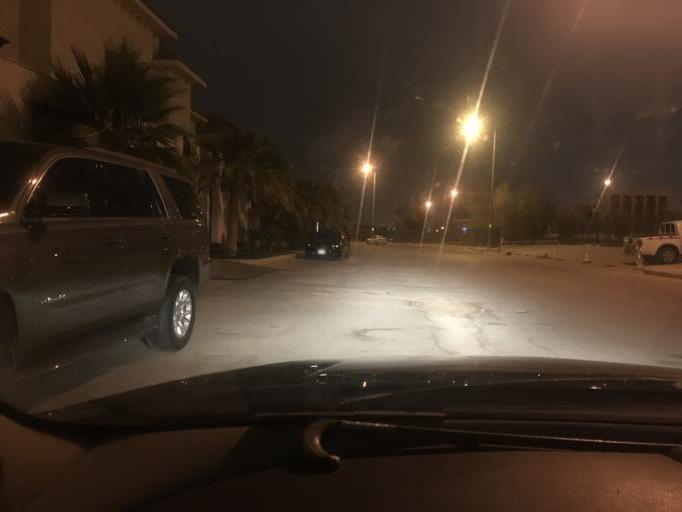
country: SA
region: Ar Riyad
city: Riyadh
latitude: 24.8080
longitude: 46.6762
